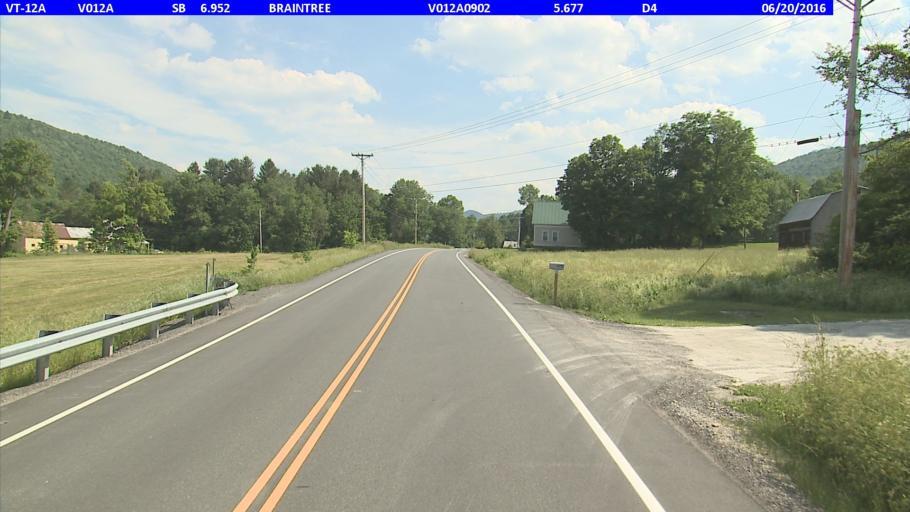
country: US
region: Vermont
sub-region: Orange County
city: Randolph
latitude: 43.9891
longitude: -72.7528
